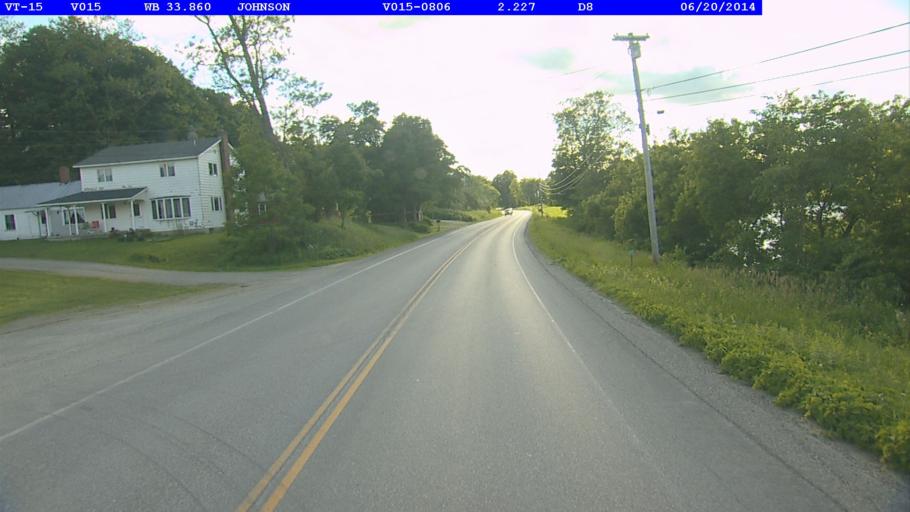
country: US
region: Vermont
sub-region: Lamoille County
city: Johnson
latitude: 44.6426
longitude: -72.7124
